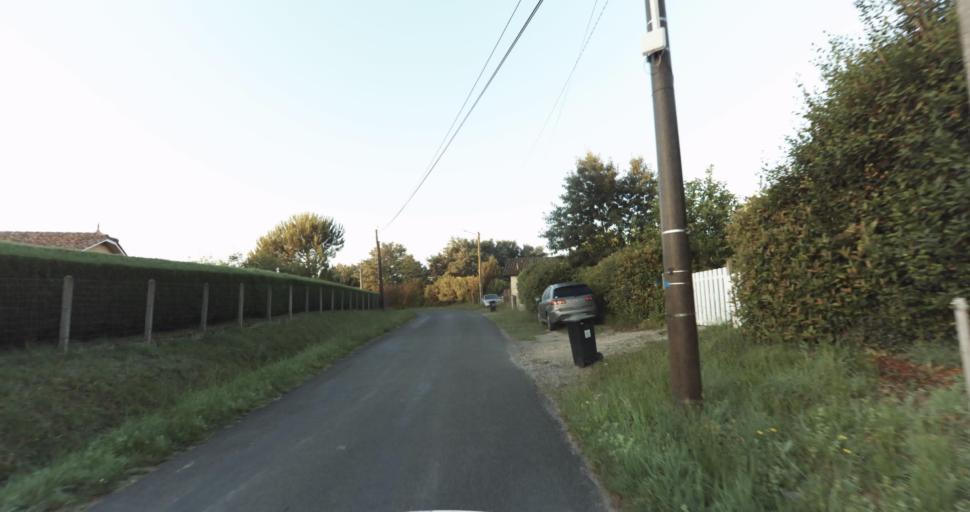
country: FR
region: Aquitaine
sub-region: Departement de la Gironde
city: Bazas
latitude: 44.4205
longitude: -0.2067
